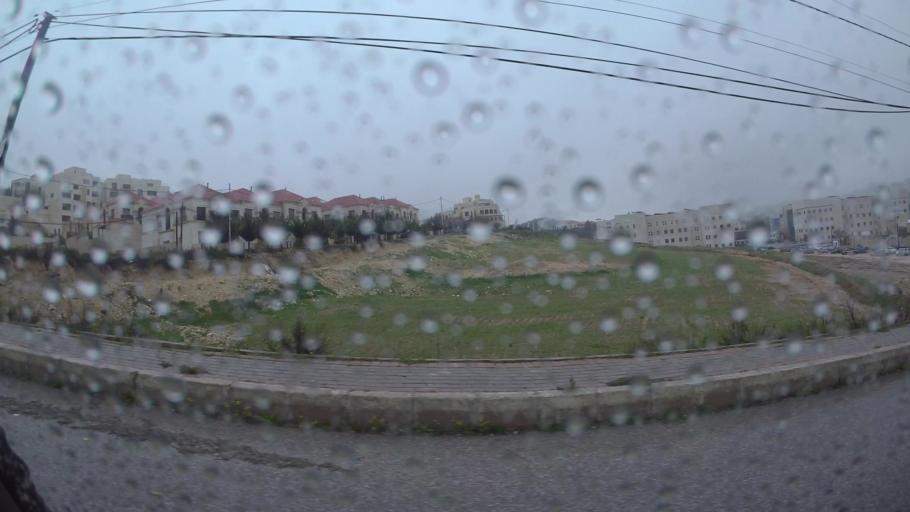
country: JO
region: Amman
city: Al Jubayhah
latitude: 32.0060
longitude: 35.8306
